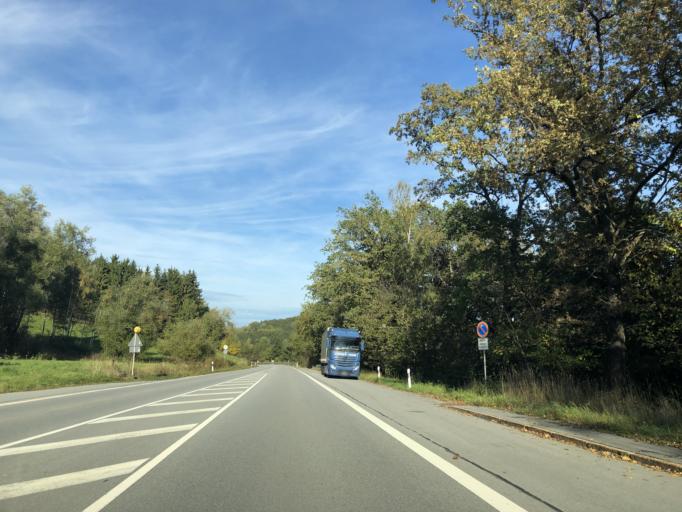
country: DE
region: Bavaria
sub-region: Lower Bavaria
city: Gotteszell
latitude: 48.9593
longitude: 12.9770
